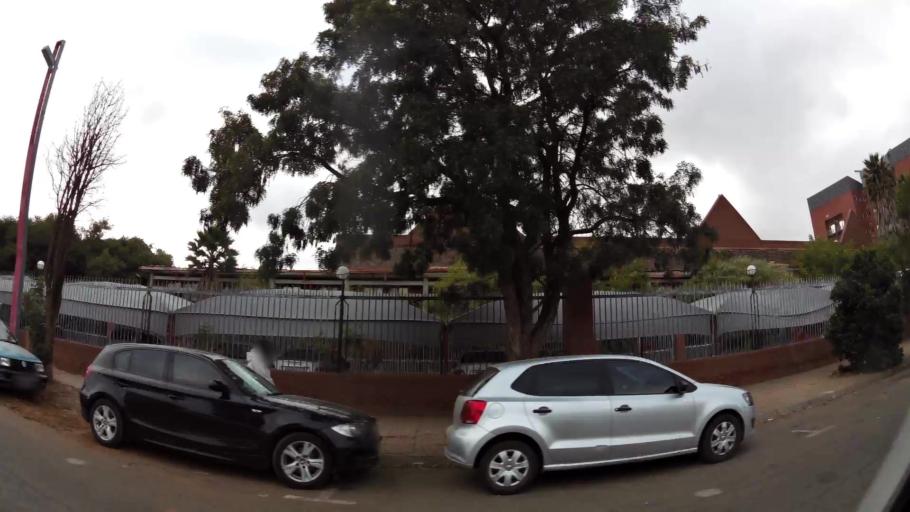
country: ZA
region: Limpopo
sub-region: Capricorn District Municipality
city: Polokwane
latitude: -23.9145
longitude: 29.4538
